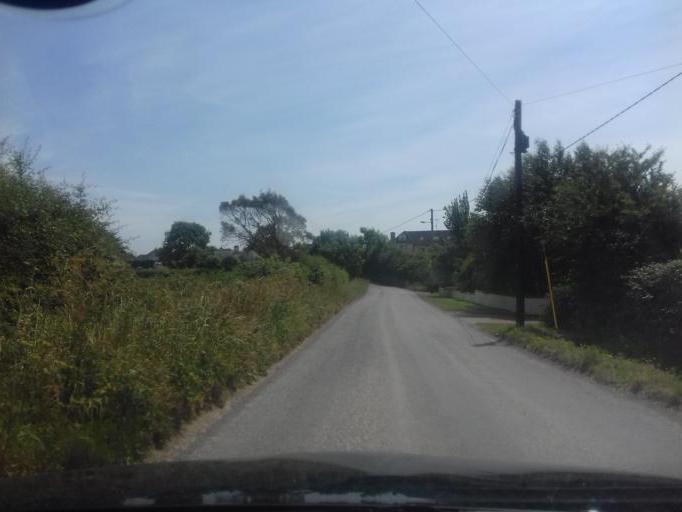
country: IE
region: Leinster
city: Lusk
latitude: 53.5332
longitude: -6.1771
